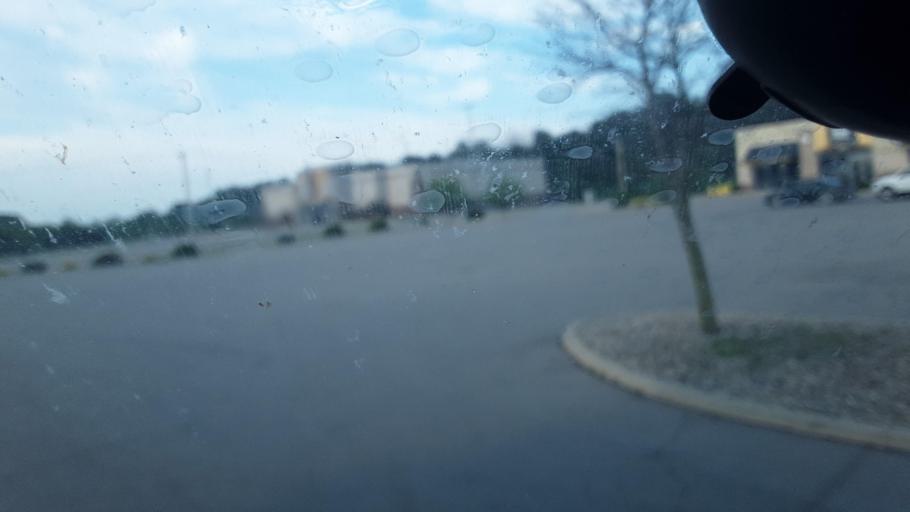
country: US
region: Indiana
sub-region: DeKalb County
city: Auburn
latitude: 41.3611
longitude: -85.0861
